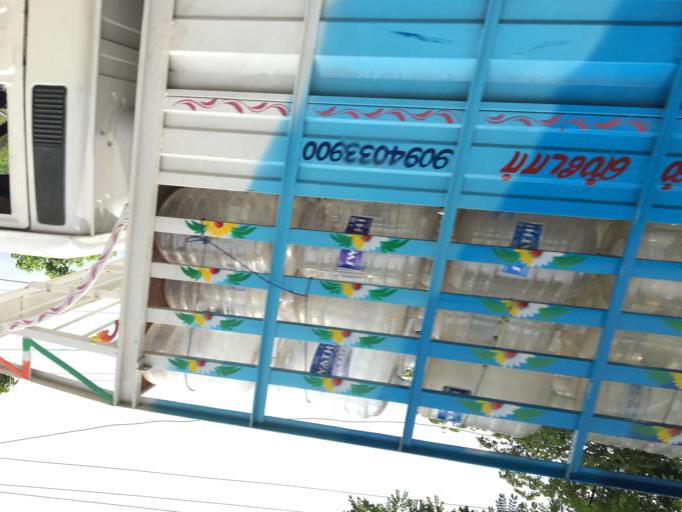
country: IN
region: Tamil Nadu
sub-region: Kancheepuram
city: Madipakkam
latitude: 12.9565
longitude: 80.2132
